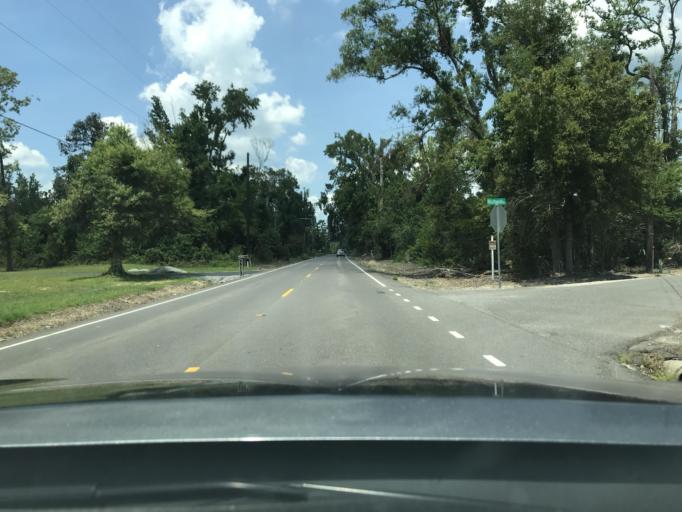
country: US
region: Louisiana
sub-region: Calcasieu Parish
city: Moss Bluff
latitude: 30.3158
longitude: -93.1834
